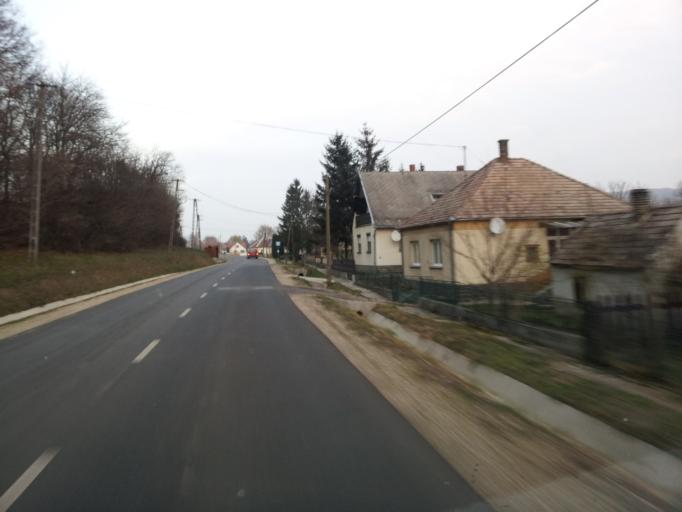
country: HU
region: Zala
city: Zalaszentgrot
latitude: 46.8905
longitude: 17.1512
